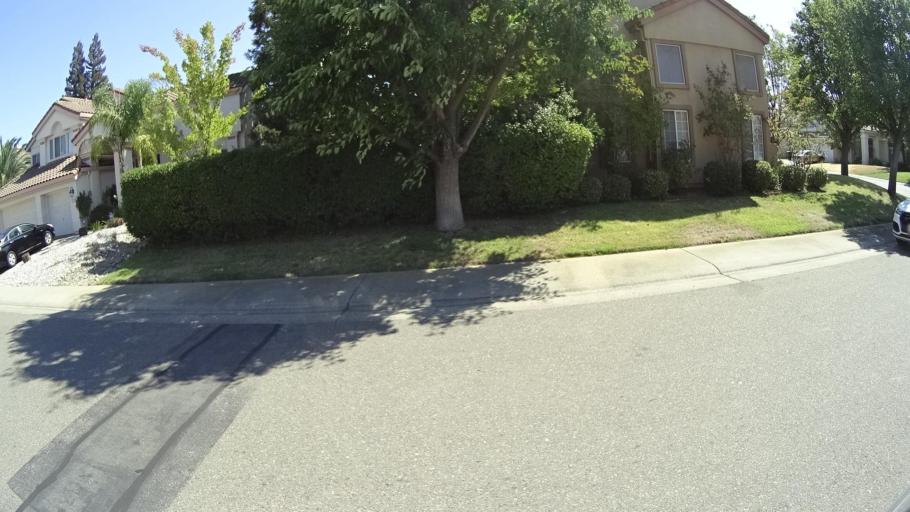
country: US
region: California
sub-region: Sacramento County
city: Laguna
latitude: 38.4132
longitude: -121.4109
